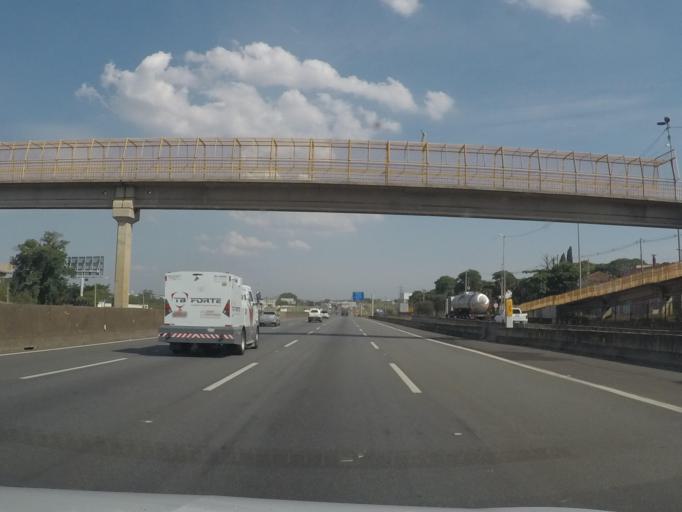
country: BR
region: Sao Paulo
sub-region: Sumare
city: Sumare
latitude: -22.8046
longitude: -47.2190
